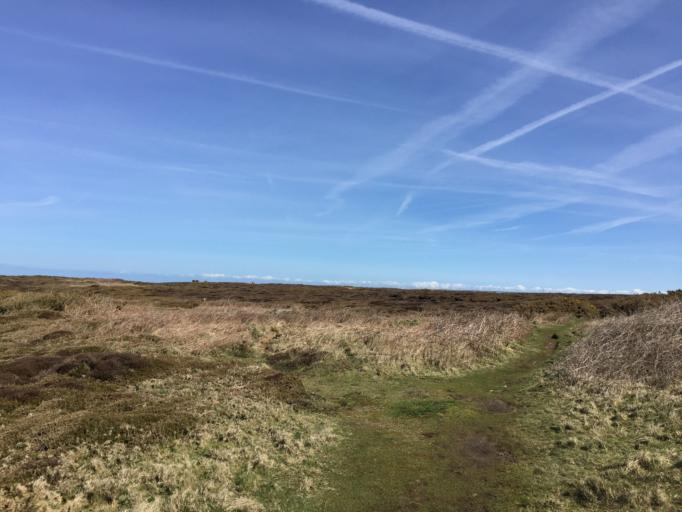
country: JE
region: St Helier
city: Saint Helier
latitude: 49.2525
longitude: -2.2499
